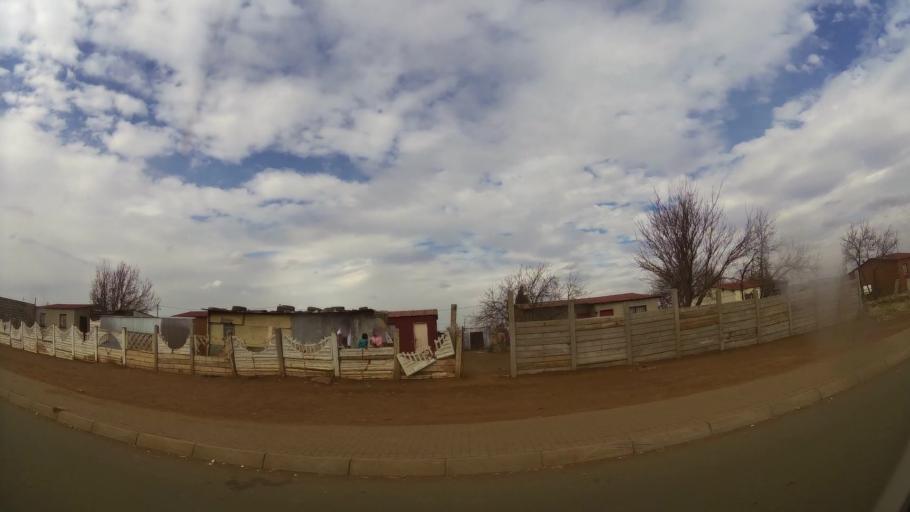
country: ZA
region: Gauteng
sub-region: Ekurhuleni Metropolitan Municipality
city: Germiston
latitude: -26.4074
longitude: 28.1533
